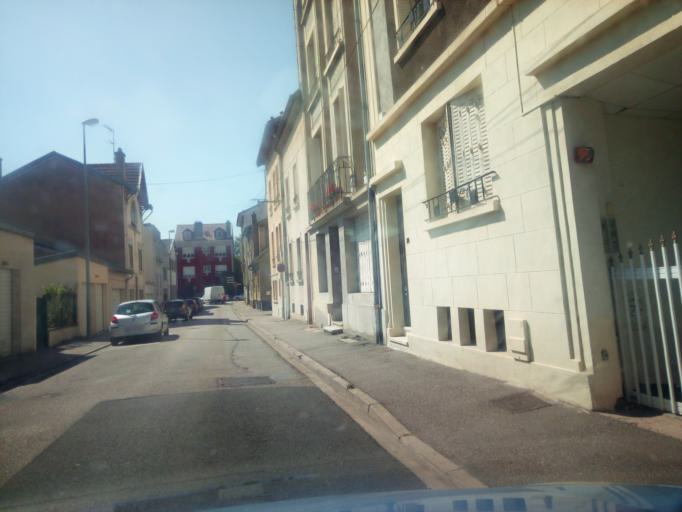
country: FR
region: Lorraine
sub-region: Departement de Meurthe-et-Moselle
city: Saint-Max
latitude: 48.6997
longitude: 6.2076
